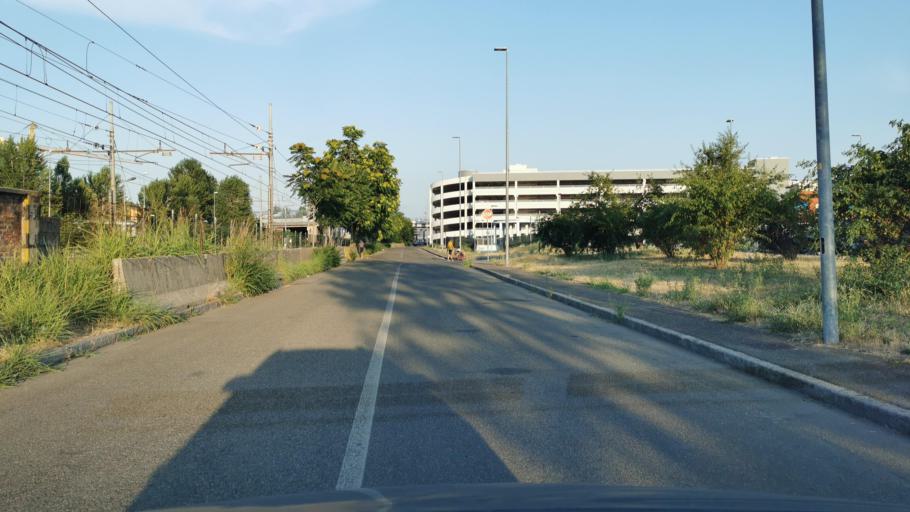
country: IT
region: Emilia-Romagna
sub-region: Provincia di Modena
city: Modena
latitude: 44.6518
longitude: 10.9385
